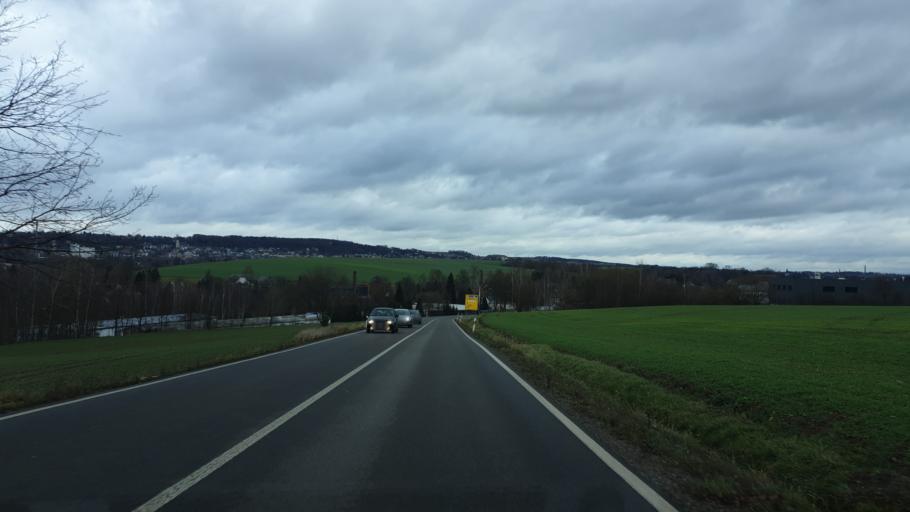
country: DE
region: Saxony
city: Oberlungwitz
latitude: 50.7780
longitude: 12.6920
